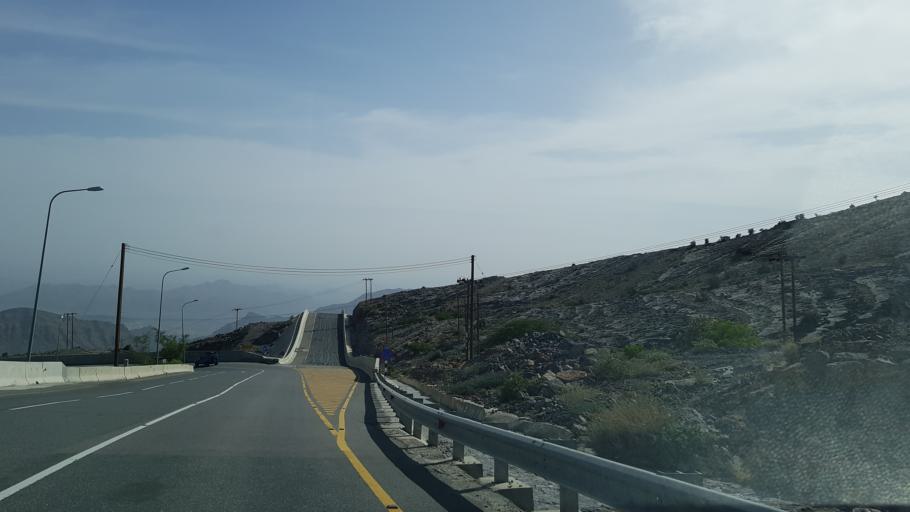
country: OM
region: Muhafazat ad Dakhiliyah
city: Izki
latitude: 23.0055
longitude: 57.6984
